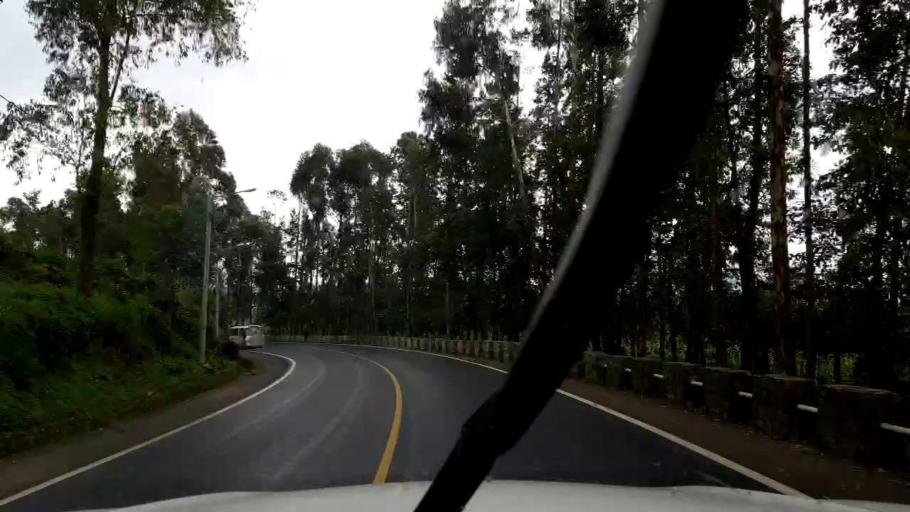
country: RW
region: Western Province
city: Gisenyi
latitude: -1.6731
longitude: 29.3579
